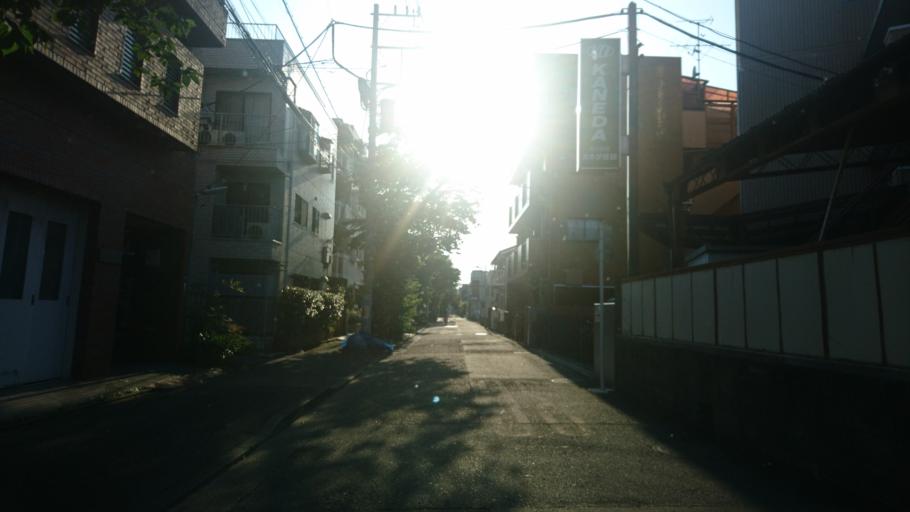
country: JP
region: Kanagawa
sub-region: Kawasaki-shi
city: Kawasaki
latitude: 35.5755
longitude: 139.7202
